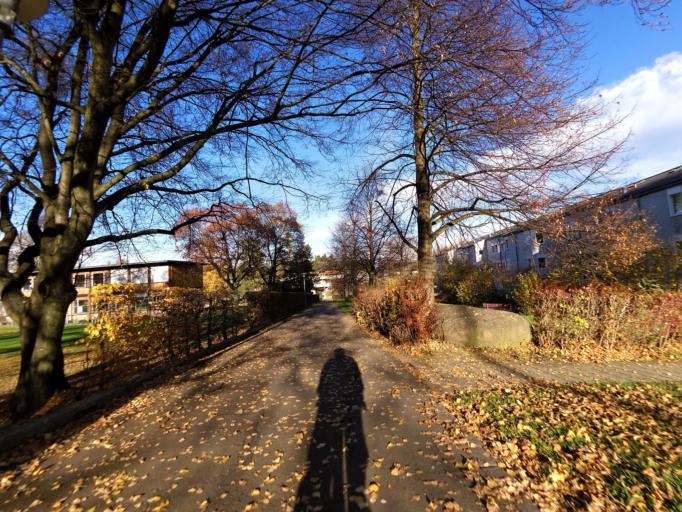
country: CH
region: Zurich
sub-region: Bezirk Zuerich
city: Zuerich (Kreis 9) / Albisrieden
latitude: 47.3730
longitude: 8.4886
